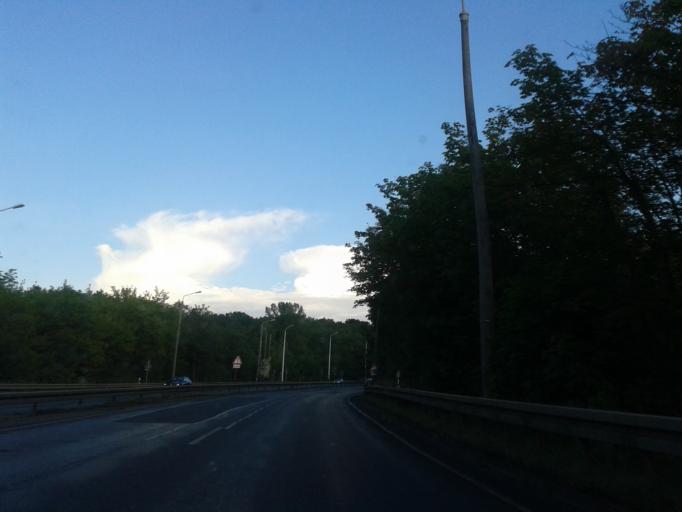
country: DE
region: Saxony
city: Markkleeberg
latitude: 51.3012
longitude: 12.3744
